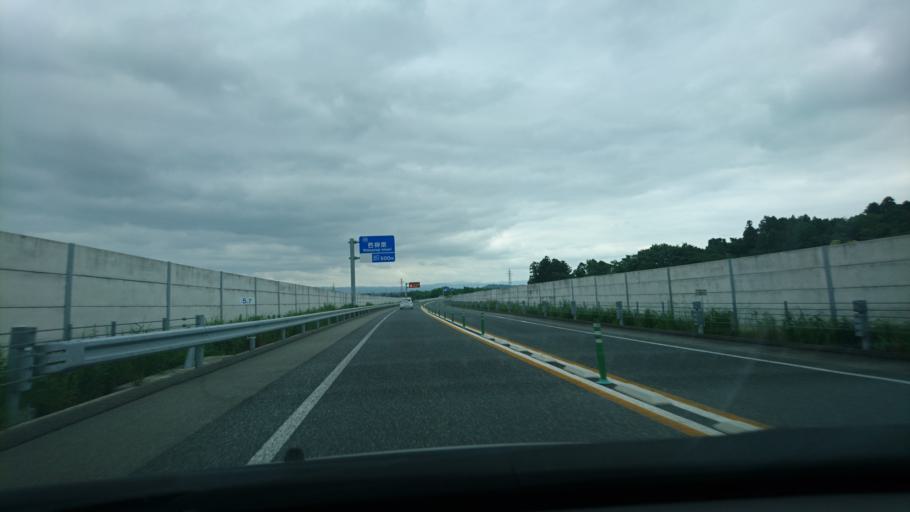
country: JP
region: Iwate
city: Ichinoseki
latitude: 38.7379
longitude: 141.1208
